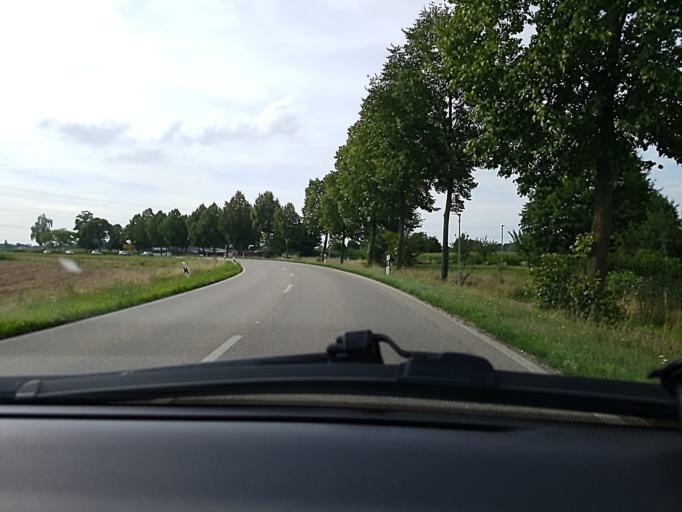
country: DE
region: Baden-Wuerttemberg
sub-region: Freiburg Region
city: Willstatt
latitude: 48.5660
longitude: 7.8633
